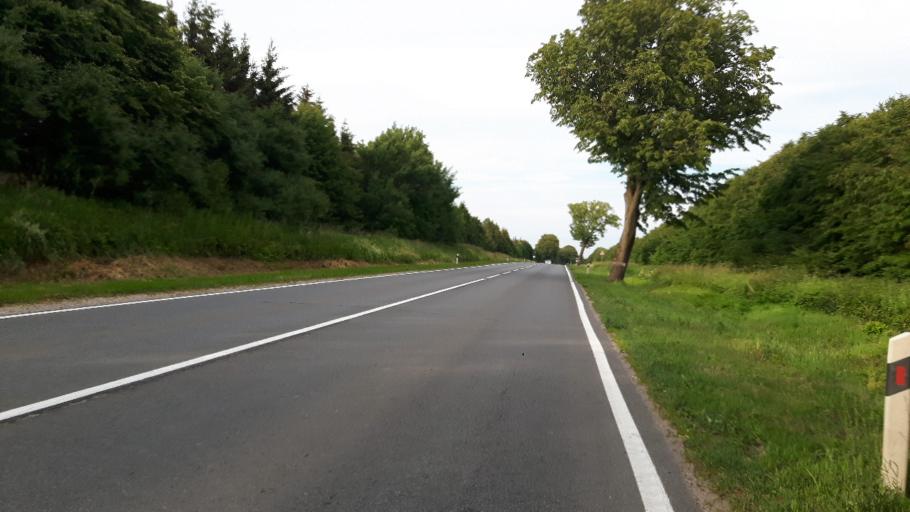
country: RU
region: Kaliningrad
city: Vzmorye
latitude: 54.6159
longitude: 20.2597
